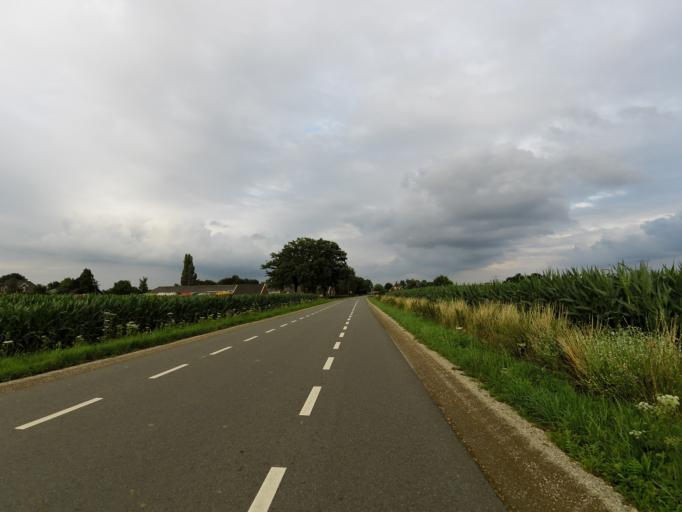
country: NL
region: Gelderland
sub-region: Gemeente Doesburg
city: Doesburg
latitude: 51.9867
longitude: 6.1918
